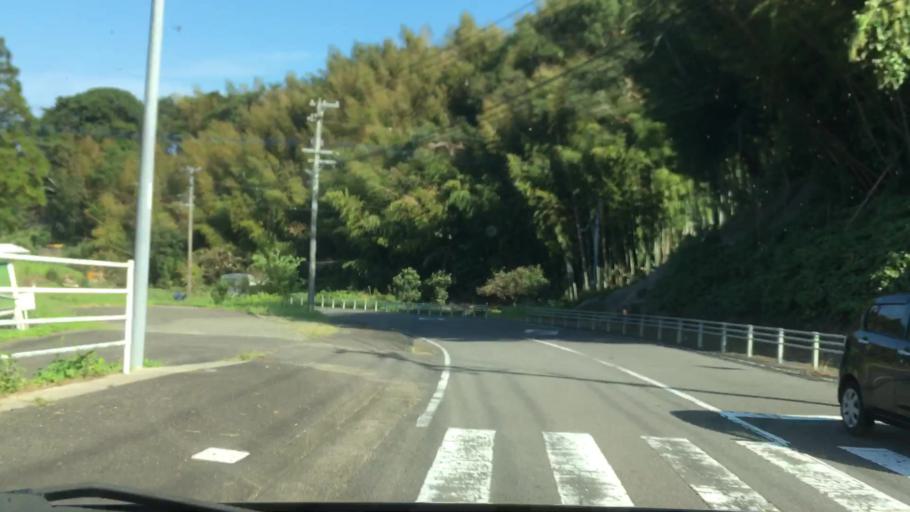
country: JP
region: Nagasaki
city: Sasebo
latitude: 33.0108
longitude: 129.6560
